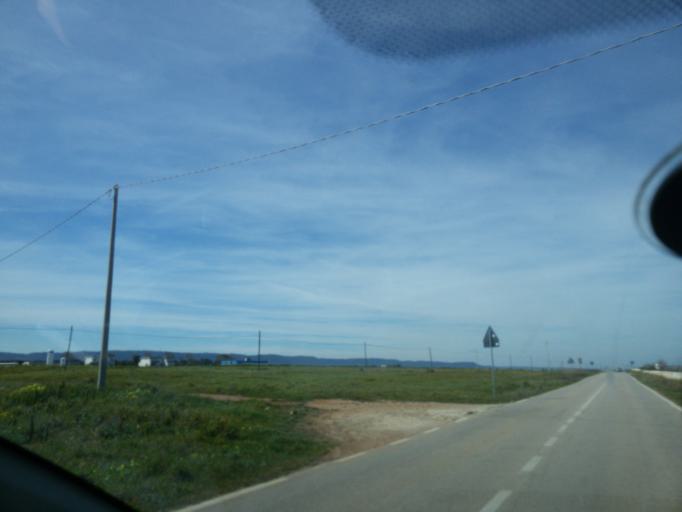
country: IT
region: Apulia
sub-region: Provincia di Brindisi
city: Pezze di Greco
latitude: 40.8471
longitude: 17.4572
